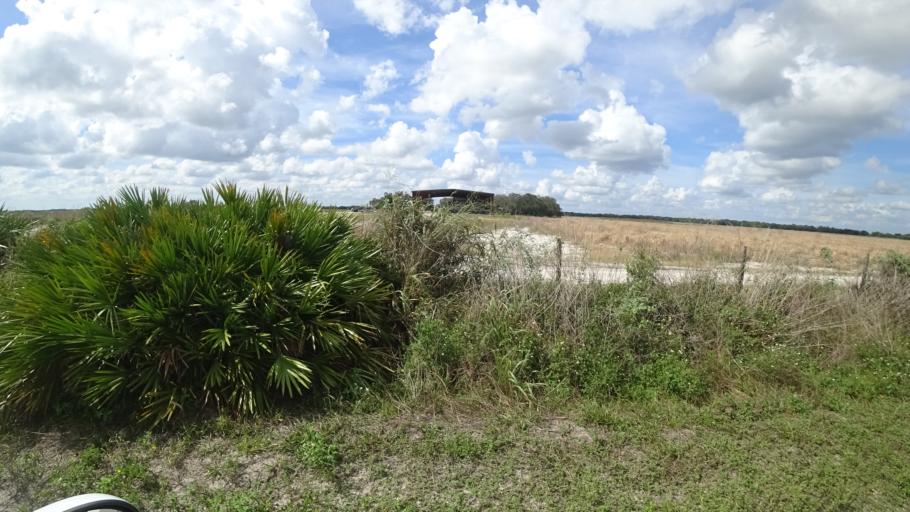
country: US
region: Florida
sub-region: Hillsborough County
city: Wimauma
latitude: 27.5867
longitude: -82.2666
